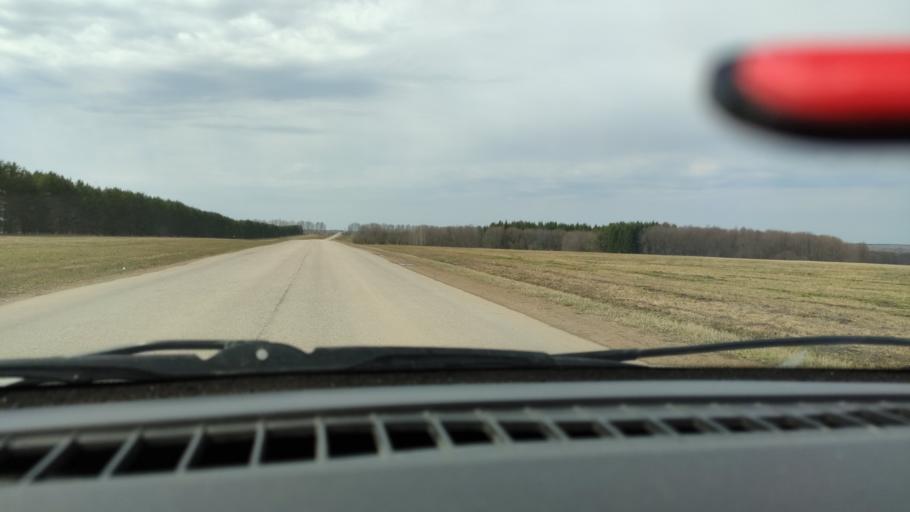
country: RU
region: Bashkortostan
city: Dyurtyuli
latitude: 55.6651
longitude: 55.0735
